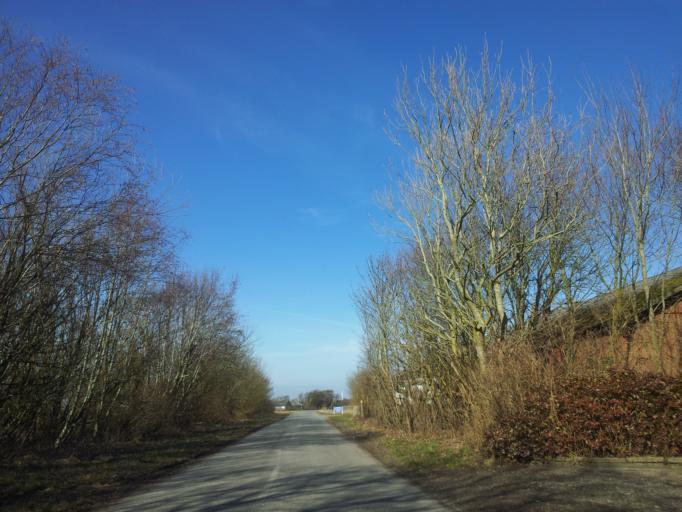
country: DK
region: South Denmark
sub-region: Tonder Kommune
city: Sherrebek
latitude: 55.1833
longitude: 8.7169
